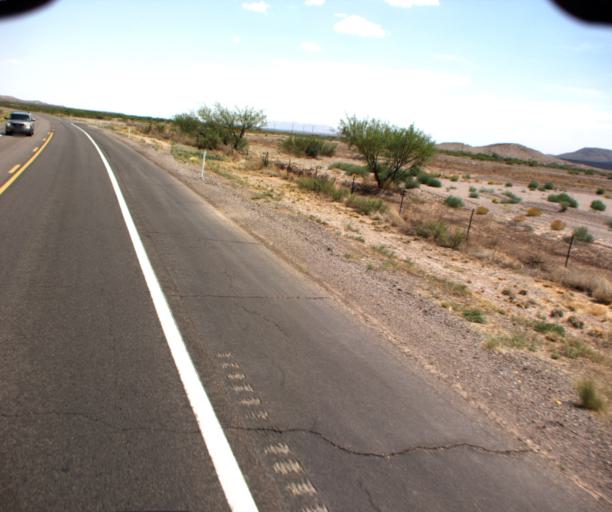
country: US
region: Arizona
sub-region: Greenlee County
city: Clifton
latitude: 32.6652
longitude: -109.0738
